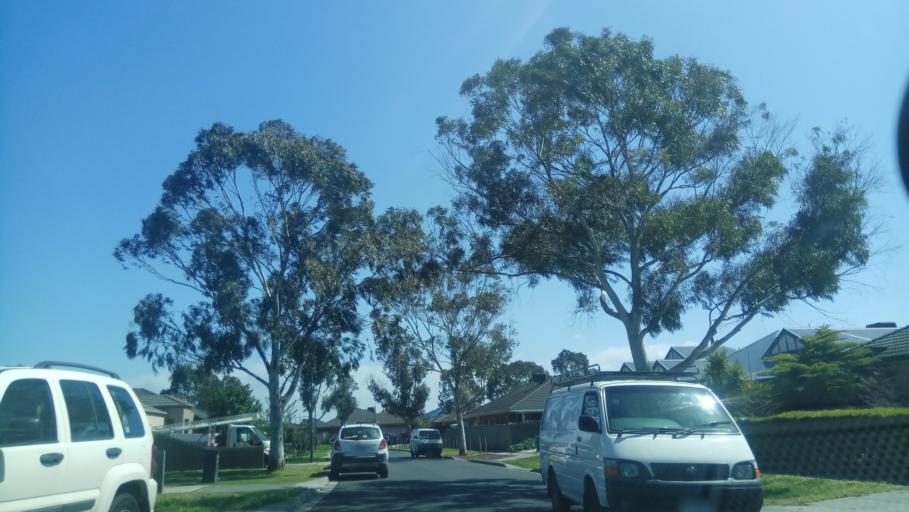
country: AU
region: Victoria
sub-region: Casey
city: Lynbrook
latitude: -38.0626
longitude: 145.2577
